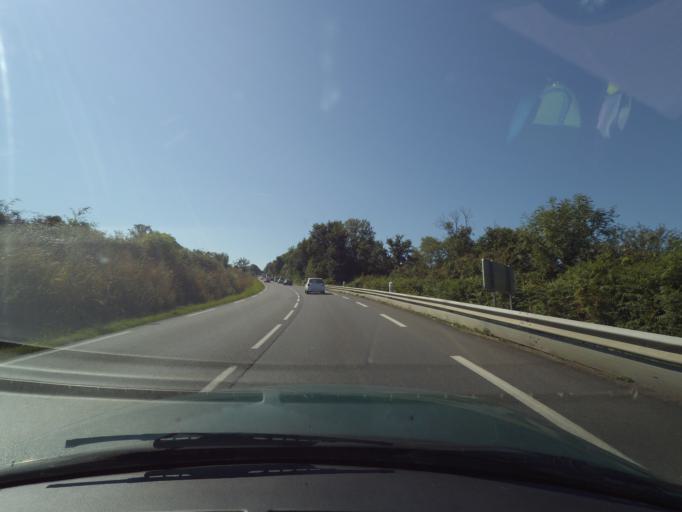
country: FR
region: Limousin
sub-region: Departement de la Haute-Vienne
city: Peyrat-de-Bellac
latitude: 46.1588
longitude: 0.9599
